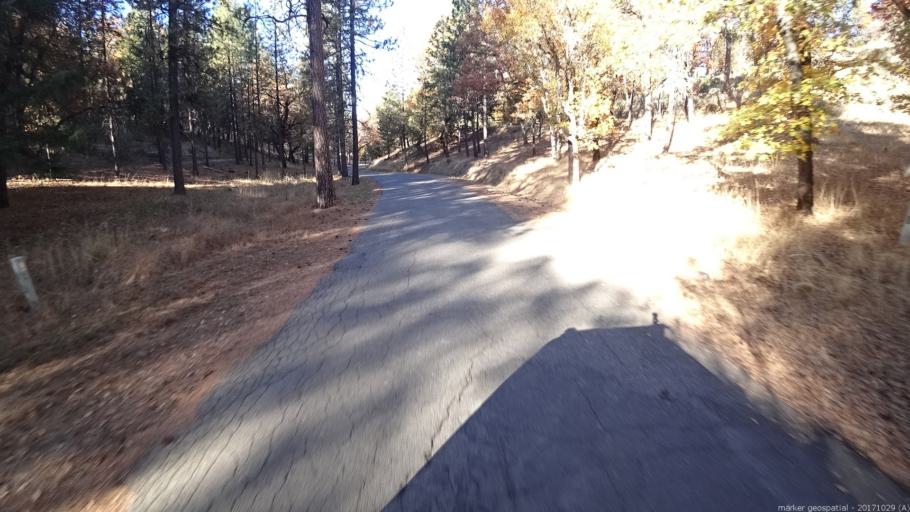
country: US
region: California
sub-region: Trinity County
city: Hayfork
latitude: 40.3628
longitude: -122.9542
